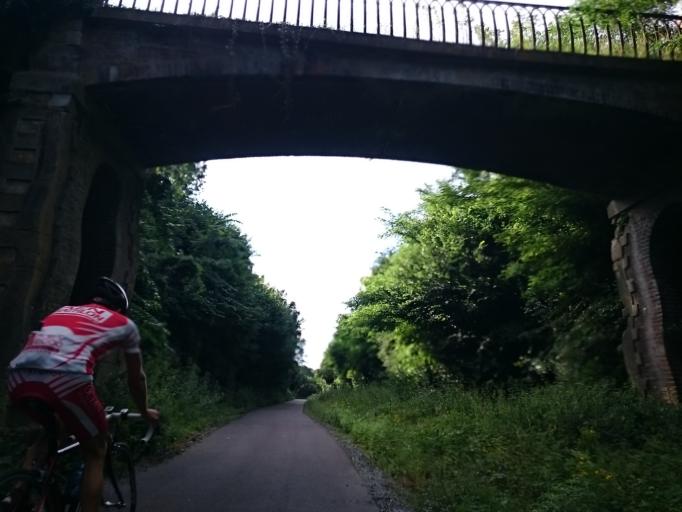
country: FR
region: Lower Normandy
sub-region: Departement du Calvados
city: Saint-Andre-sur-Orne
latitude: 49.1193
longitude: -0.3947
